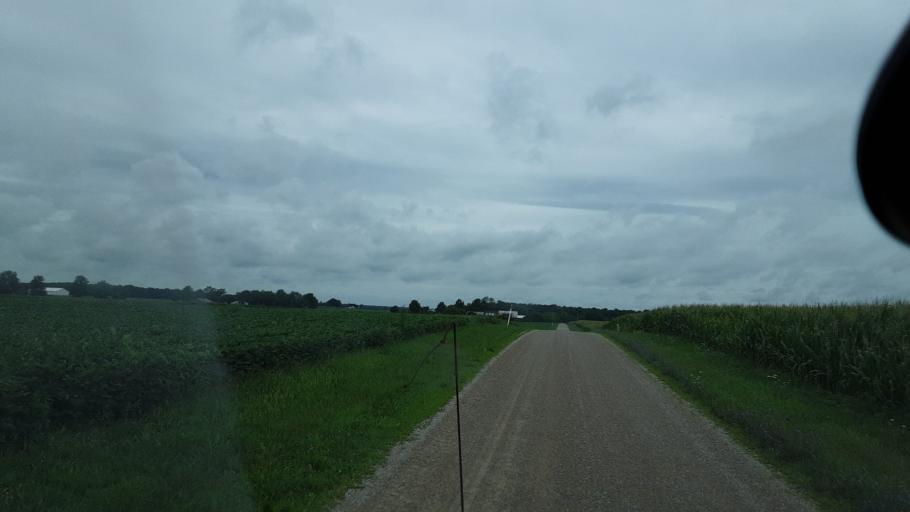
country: US
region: Indiana
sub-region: Jay County
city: Portland
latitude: 40.4905
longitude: -85.0044
